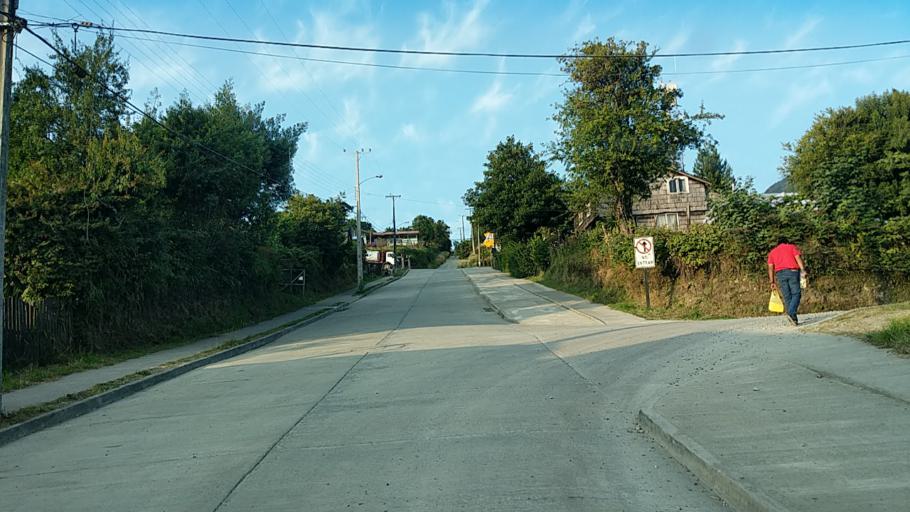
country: CL
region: Los Lagos
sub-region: Provincia de Llanquihue
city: La Ensenada
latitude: -41.4934
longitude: -72.3084
